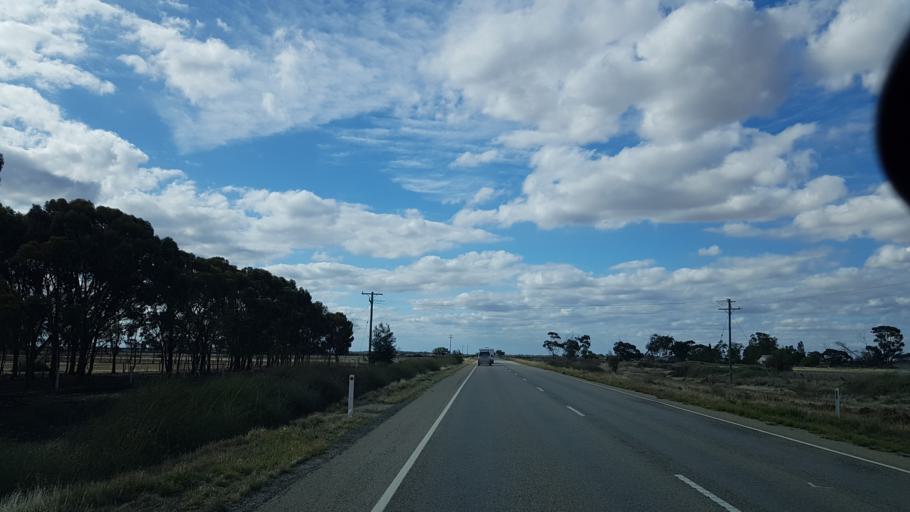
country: AU
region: Victoria
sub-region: Swan Hill
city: Swan Hill
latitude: -35.8600
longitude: 143.9353
